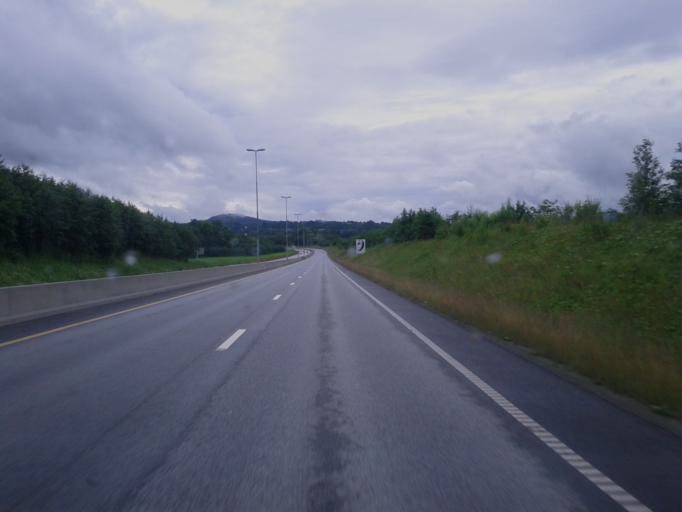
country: NO
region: Sor-Trondelag
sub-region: Melhus
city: Melhus
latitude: 63.2960
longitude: 10.2809
